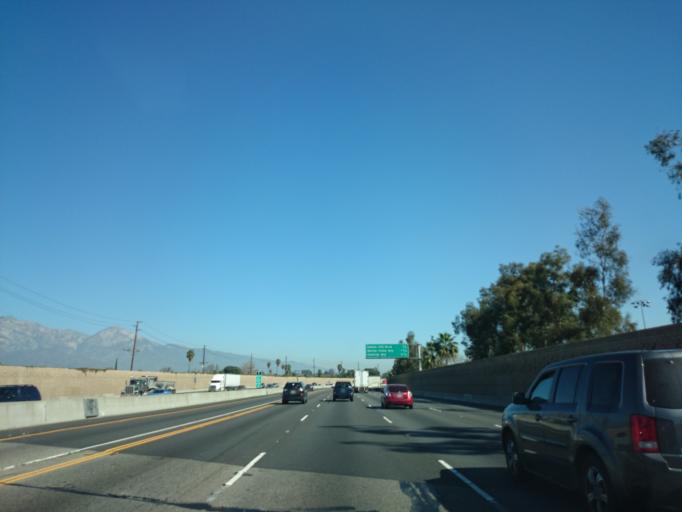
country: US
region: California
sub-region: Los Angeles County
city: Claremont
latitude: 34.0802
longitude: -117.7366
